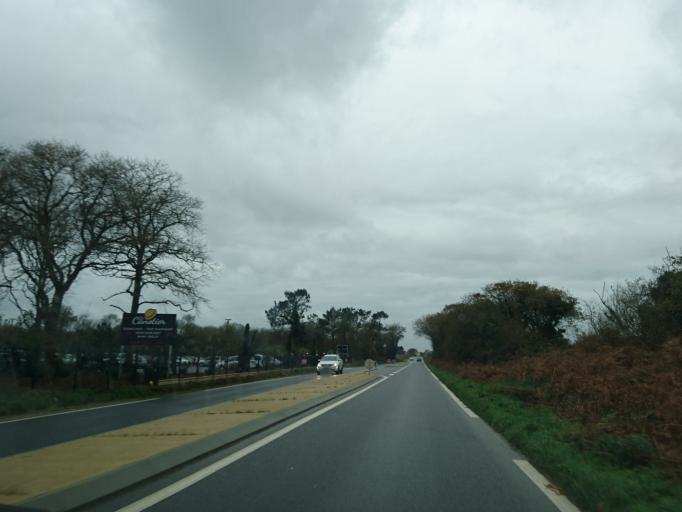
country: FR
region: Brittany
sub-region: Departement du Finistere
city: Plouzane
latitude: 48.3614
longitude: -4.6498
